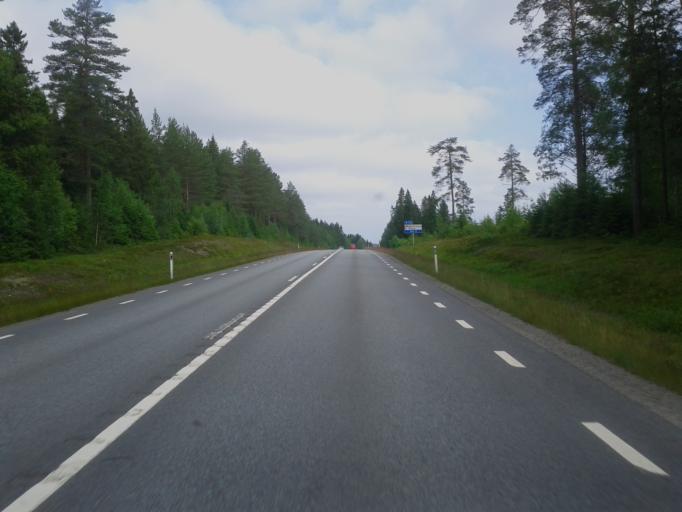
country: SE
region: Vaesterbotten
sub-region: Skelleftea Kommun
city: Burea
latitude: 64.3588
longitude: 21.2960
